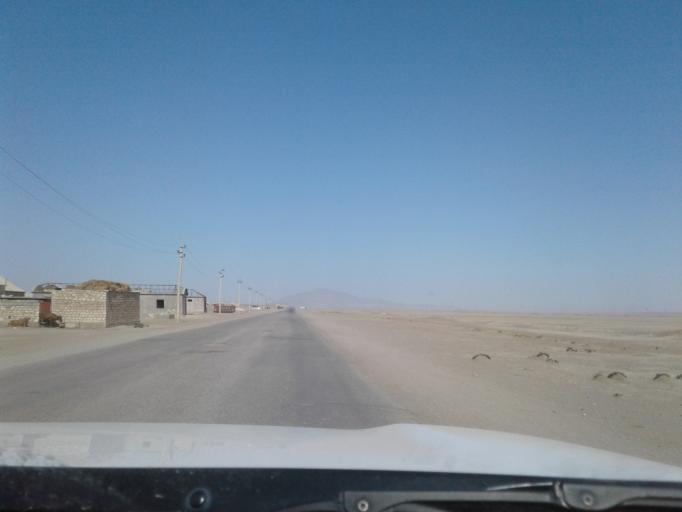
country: TM
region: Balkan
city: Gumdag
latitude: 39.1943
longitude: 54.5921
